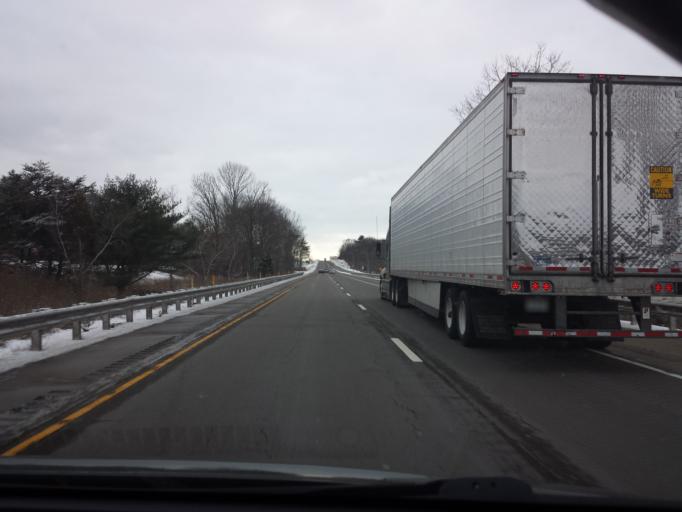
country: US
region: Pennsylvania
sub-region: Columbia County
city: Berwick
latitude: 41.0089
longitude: -76.2487
